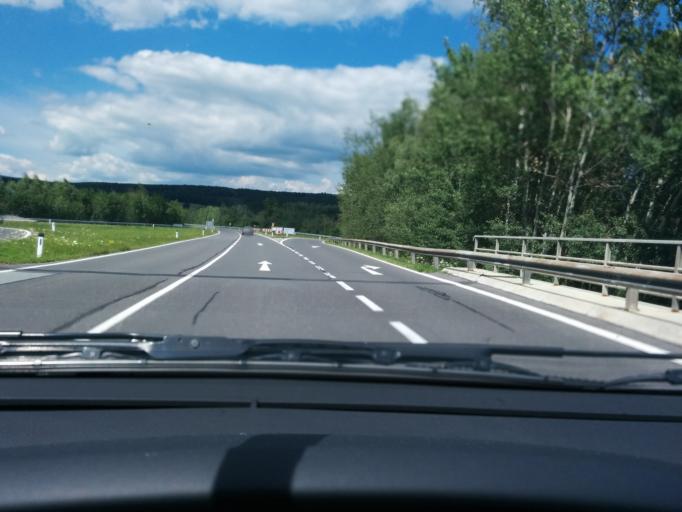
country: AT
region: Styria
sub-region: Politischer Bezirk Hartberg-Fuerstenfeld
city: Lafnitz
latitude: 47.3688
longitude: 16.0179
